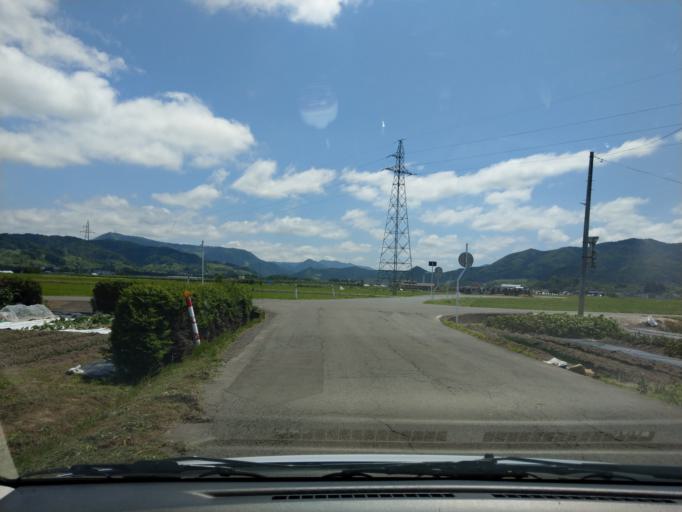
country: JP
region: Aomori
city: Hirosaki
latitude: 40.5617
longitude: 140.5516
